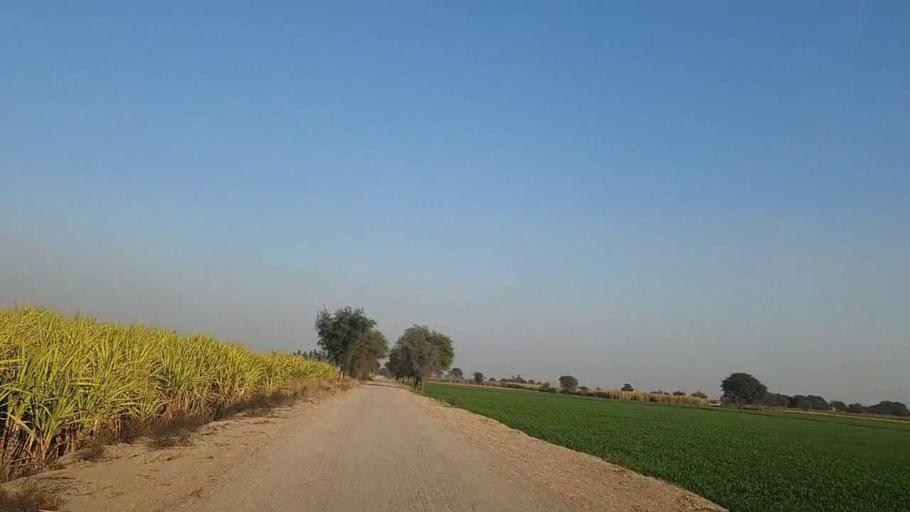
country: PK
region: Sindh
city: Sakrand
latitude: 26.3052
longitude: 68.1296
